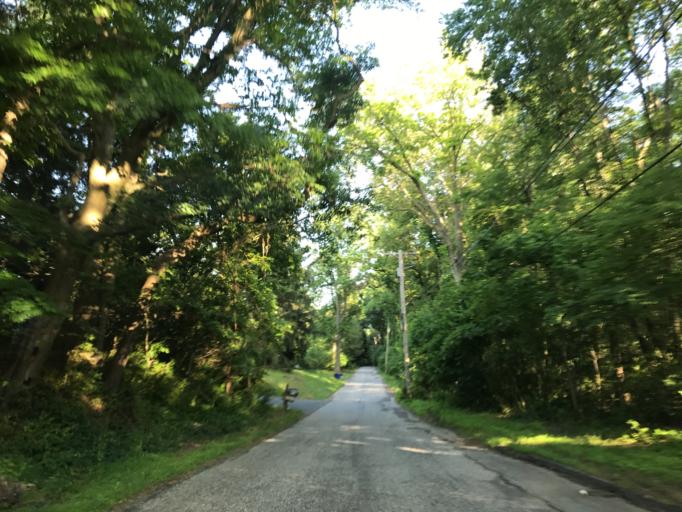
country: US
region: Maryland
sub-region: Harford County
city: Fallston
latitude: 39.5014
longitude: -76.4922
